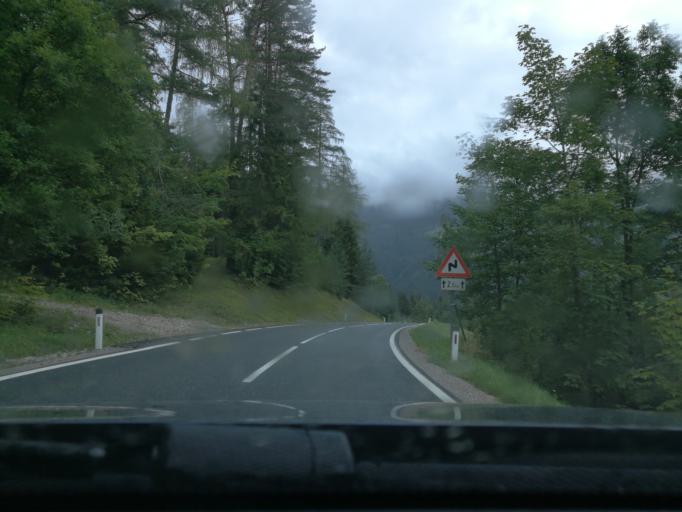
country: AT
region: Salzburg
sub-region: Politischer Bezirk Sankt Johann im Pongau
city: Forstau
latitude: 47.3823
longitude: 13.5030
